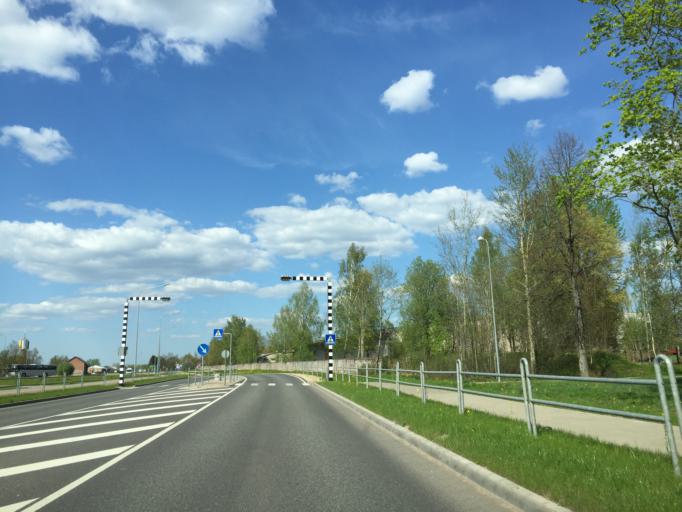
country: LV
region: Limbazu Rajons
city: Limbazi
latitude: 57.5074
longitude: 24.7221
